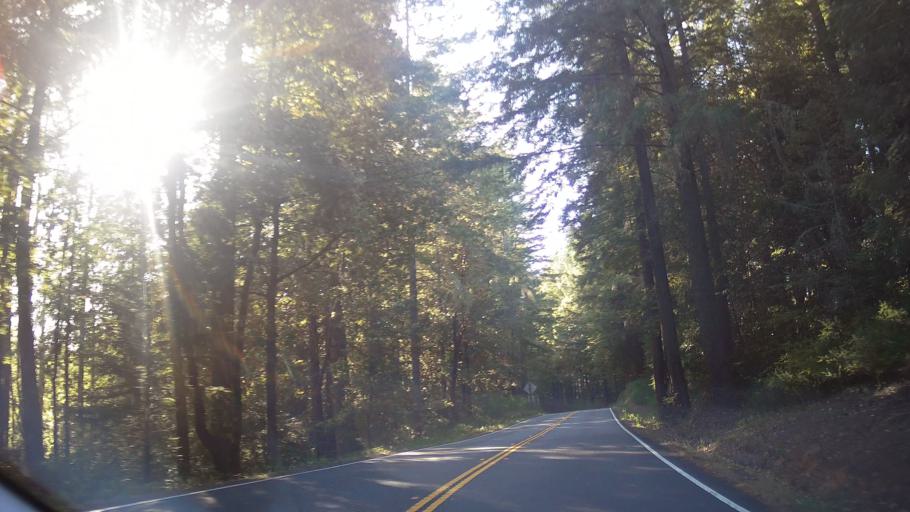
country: US
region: California
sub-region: Mendocino County
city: Fort Bragg
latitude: 39.3559
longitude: -123.6297
